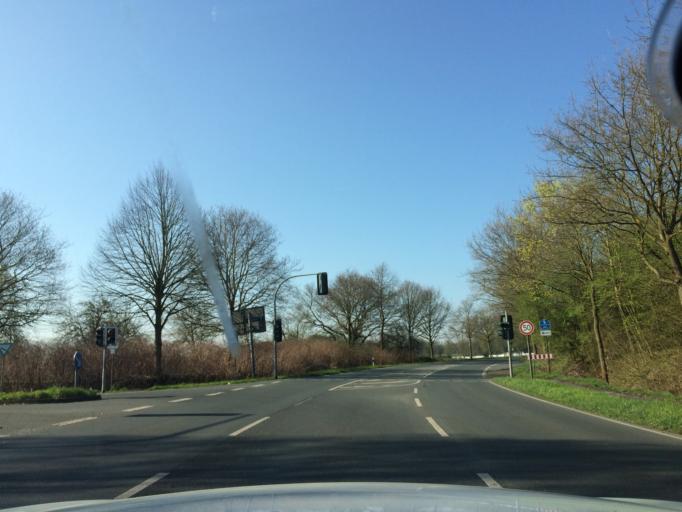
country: DE
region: North Rhine-Westphalia
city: Herten
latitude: 51.5923
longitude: 7.0955
